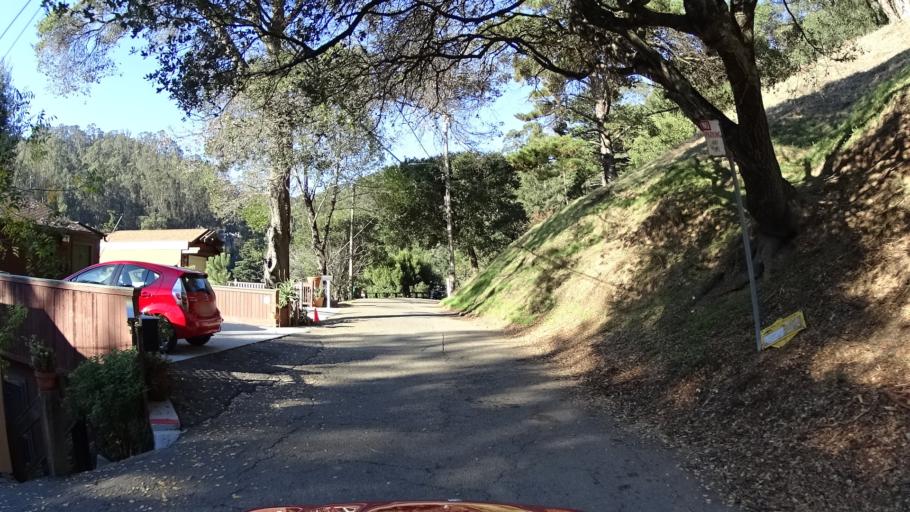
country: US
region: California
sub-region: Alameda County
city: Piedmont
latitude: 37.8444
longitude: -122.2077
